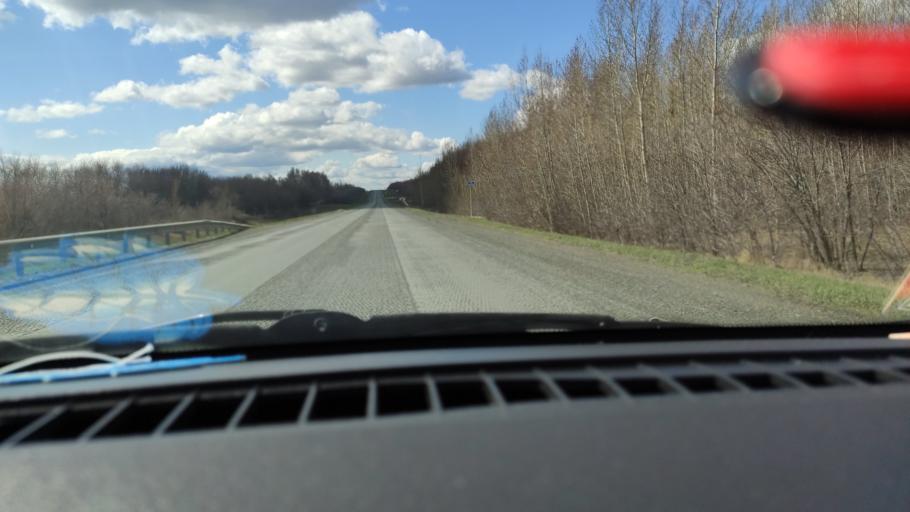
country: RU
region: Saratov
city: Dukhovnitskoye
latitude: 52.6897
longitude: 48.2424
